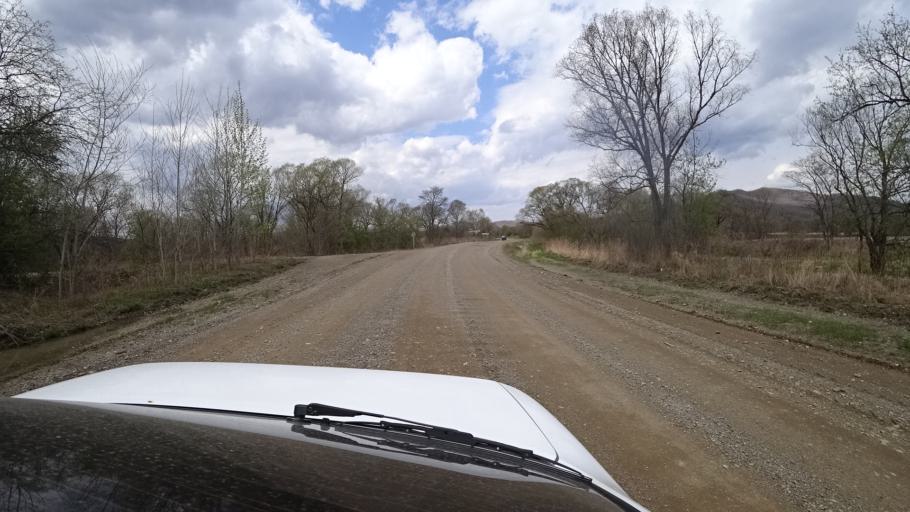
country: RU
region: Primorskiy
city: Novopokrovka
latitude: 45.6114
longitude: 134.2747
